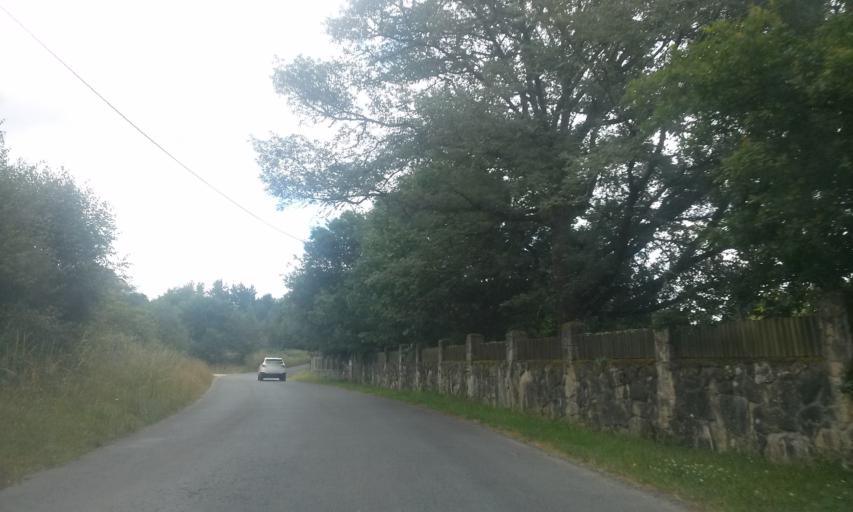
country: ES
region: Galicia
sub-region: Provincia de Lugo
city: Outeiro de Rei
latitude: 43.0650
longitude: -7.6219
